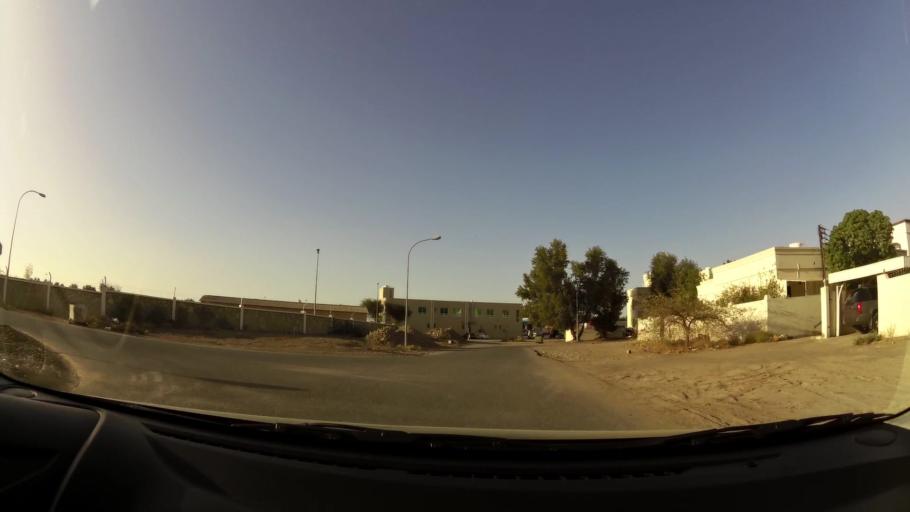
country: OM
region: Muhafazat Masqat
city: As Sib al Jadidah
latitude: 23.6109
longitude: 58.2347
